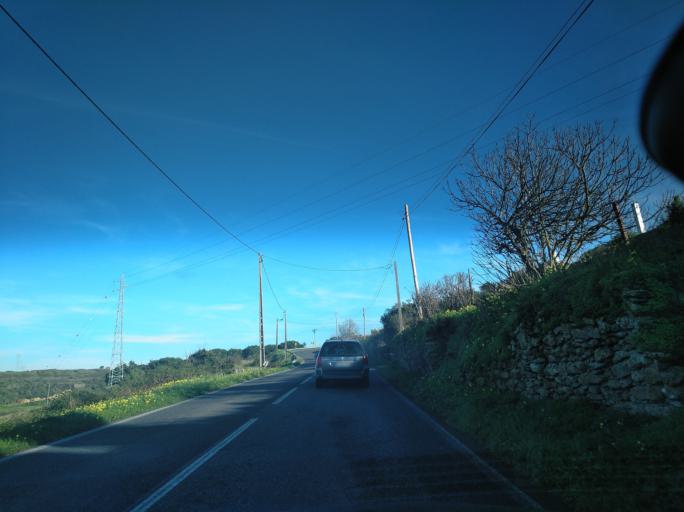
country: PT
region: Lisbon
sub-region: Sintra
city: Pero Pinheiro
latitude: 38.8826
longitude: -9.3317
